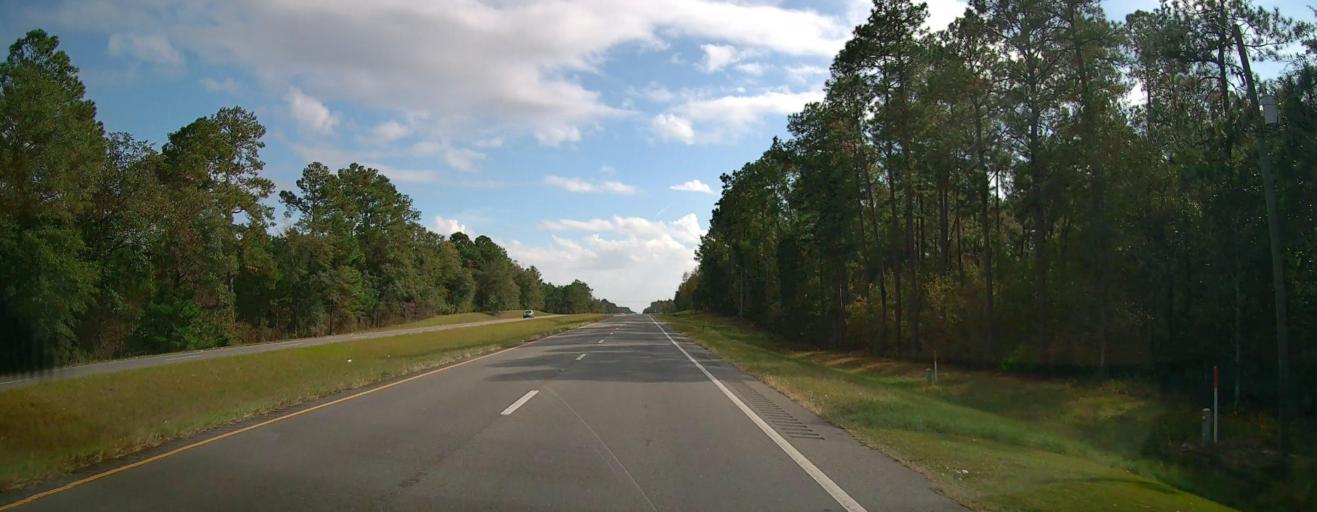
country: US
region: Georgia
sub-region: Thomas County
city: Meigs
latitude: 30.9980
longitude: -84.0470
